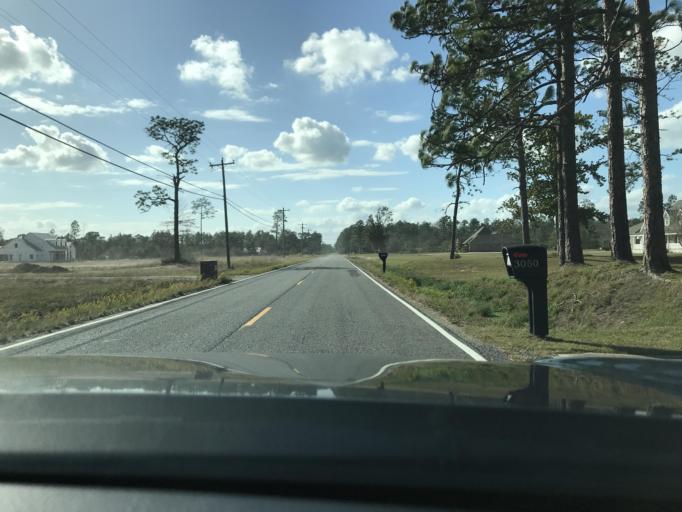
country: US
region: Louisiana
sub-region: Calcasieu Parish
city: Moss Bluff
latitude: 30.3226
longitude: -93.2640
